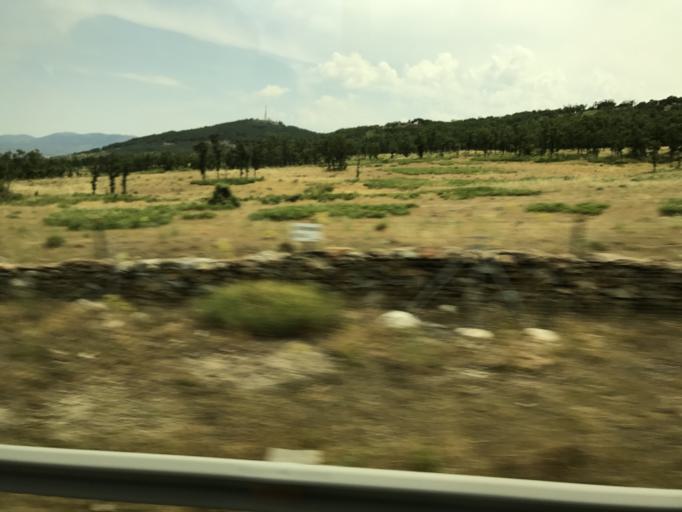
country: ES
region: Madrid
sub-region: Provincia de Madrid
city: Buitrago del Lozoya
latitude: 40.9605
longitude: -3.6416
